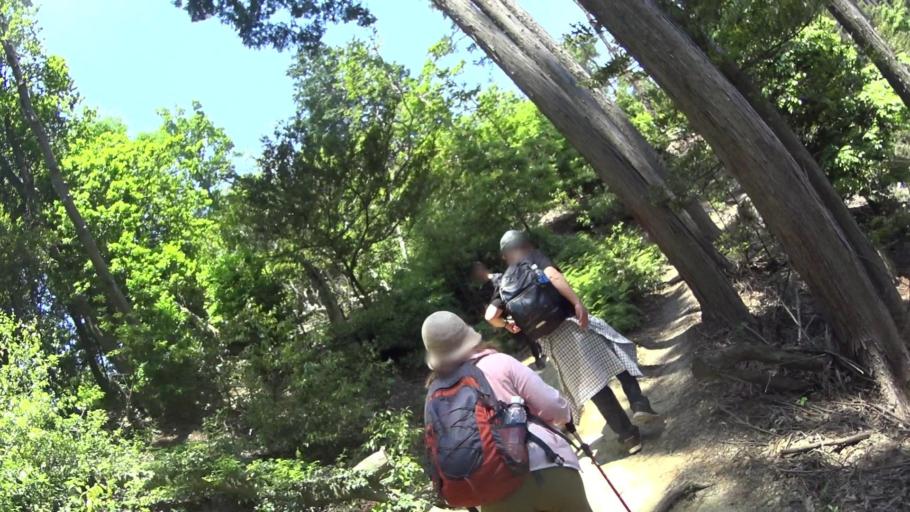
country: JP
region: Kyoto
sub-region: Kyoto-shi
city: Kamigyo-ku
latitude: 35.0164
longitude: 135.8112
